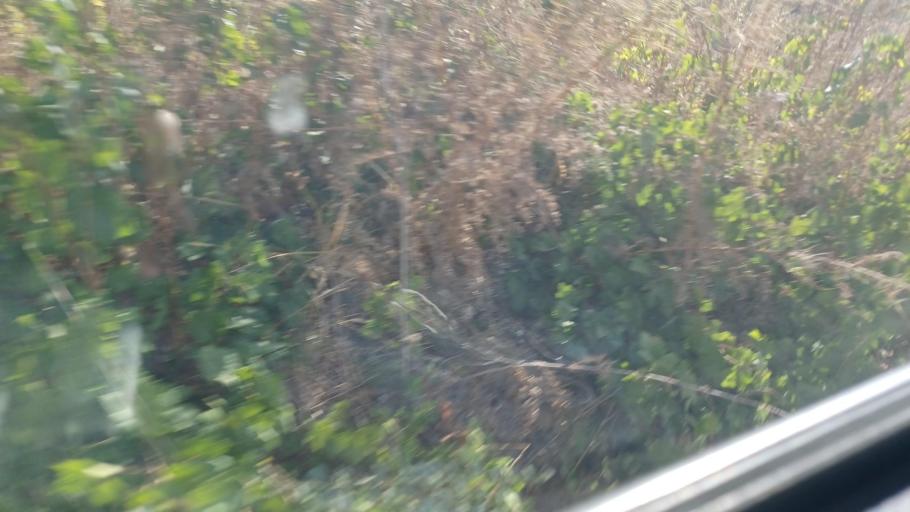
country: CY
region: Pafos
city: Mesogi
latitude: 34.8794
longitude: 32.5317
